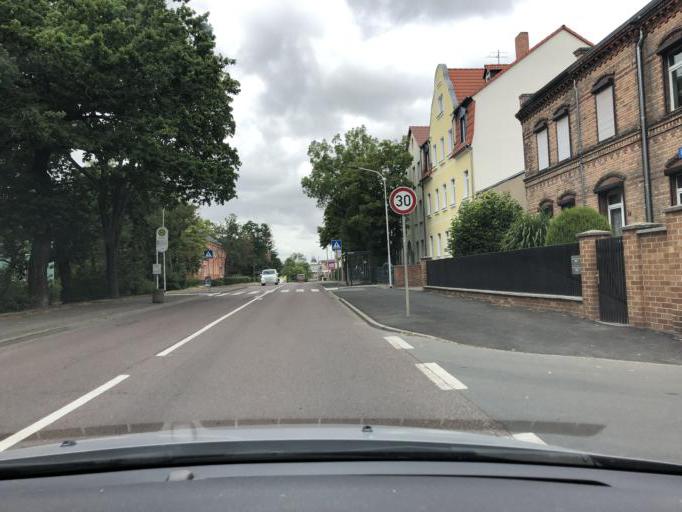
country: DE
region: Saxony-Anhalt
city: Schkopau
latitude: 51.4237
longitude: 11.9927
